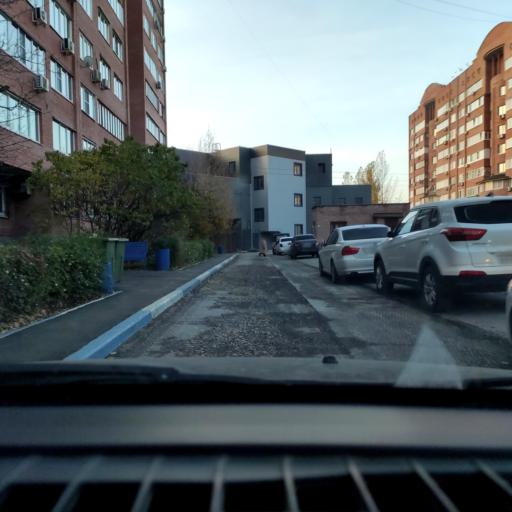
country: RU
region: Samara
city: Tol'yatti
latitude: 53.5349
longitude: 49.3470
